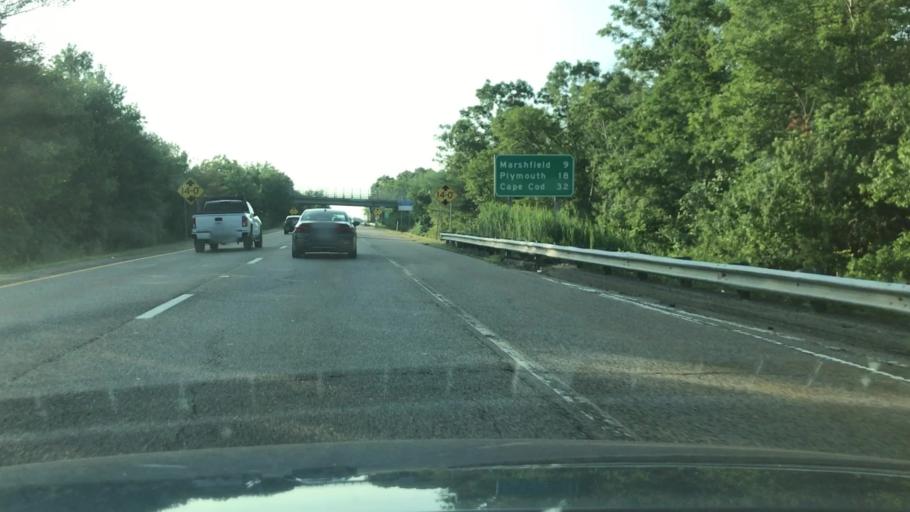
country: US
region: Massachusetts
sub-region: Plymouth County
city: Hanover
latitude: 42.1465
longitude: -70.8365
